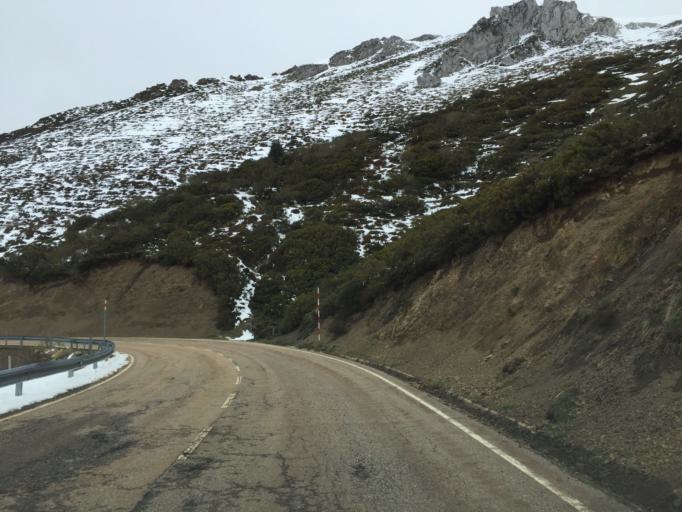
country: ES
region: Castille and Leon
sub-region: Provincia de Leon
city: San Emiliano
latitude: 43.0572
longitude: -6.0056
